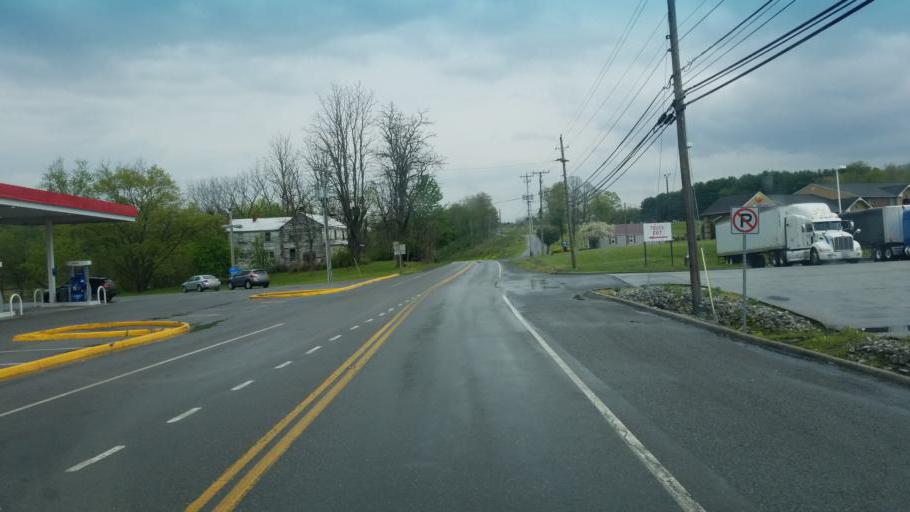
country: US
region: Virginia
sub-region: Smyth County
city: Atkins
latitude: 36.8649
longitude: -81.4345
